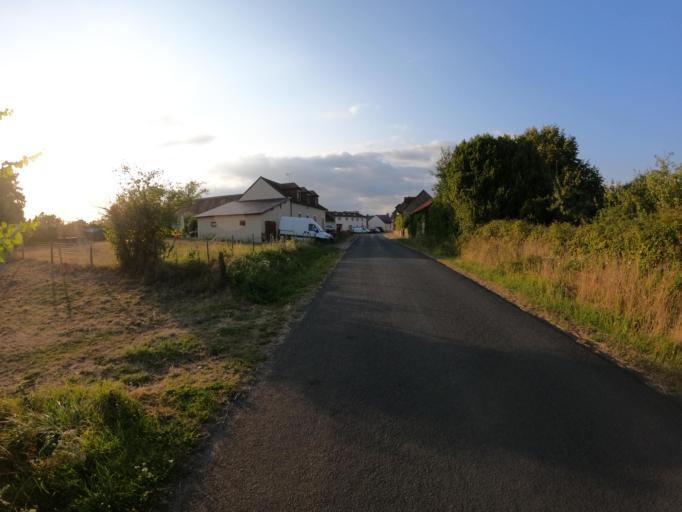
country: FR
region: Pays de la Loire
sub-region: Departement de la Sarthe
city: Brulon
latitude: 47.9467
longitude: -0.2236
